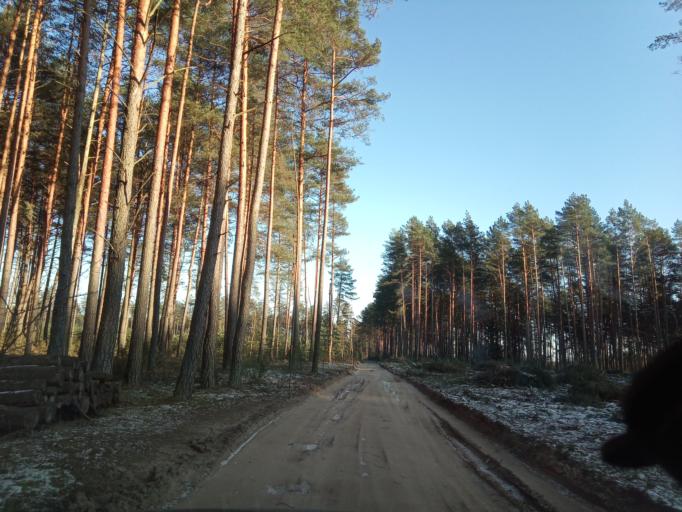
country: LT
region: Alytaus apskritis
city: Druskininkai
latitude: 53.9566
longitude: 23.8761
